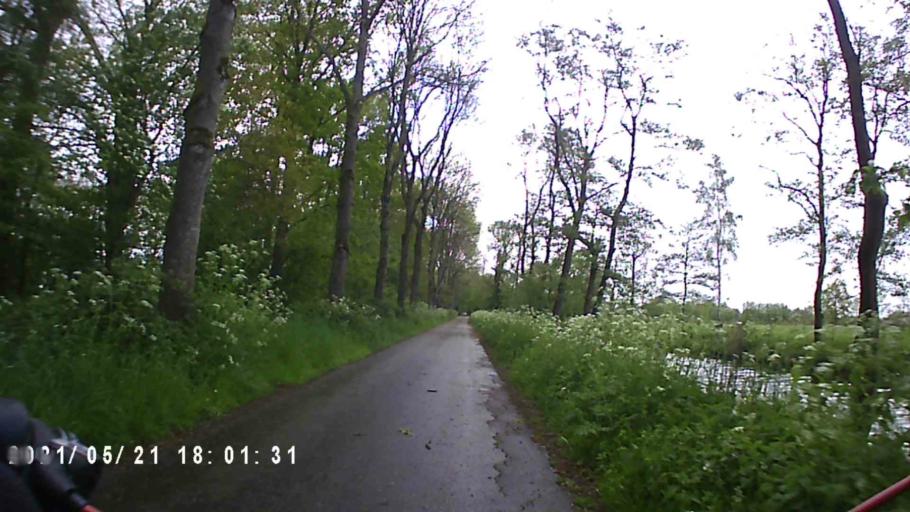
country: NL
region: Groningen
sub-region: Gemeente Leek
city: Leek
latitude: 53.1882
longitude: 6.4172
